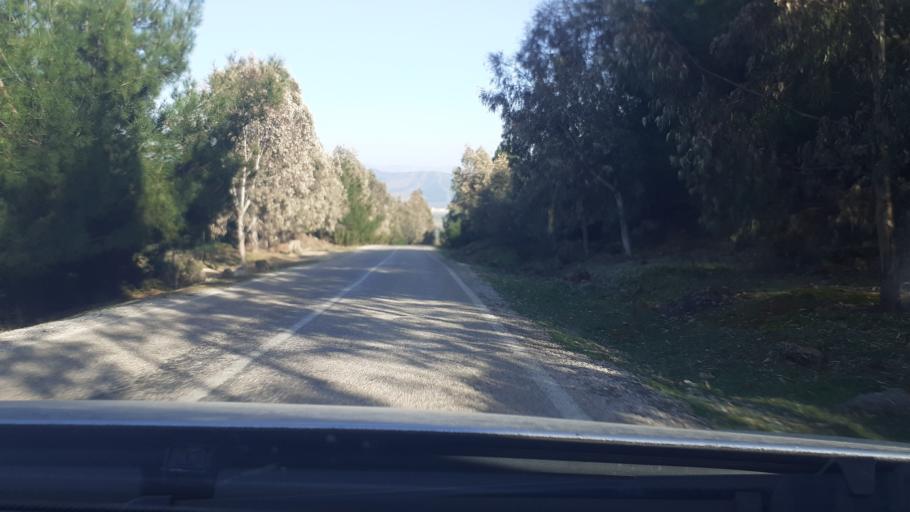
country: TR
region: Hatay
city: Aktepe
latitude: 36.7328
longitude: 36.4739
